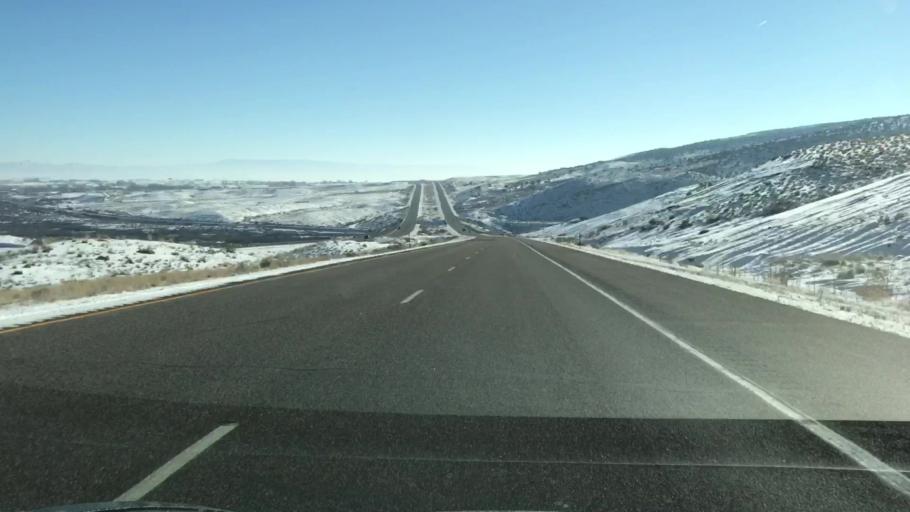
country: US
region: Colorado
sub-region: Mesa County
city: Loma
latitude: 39.2263
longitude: -108.8985
